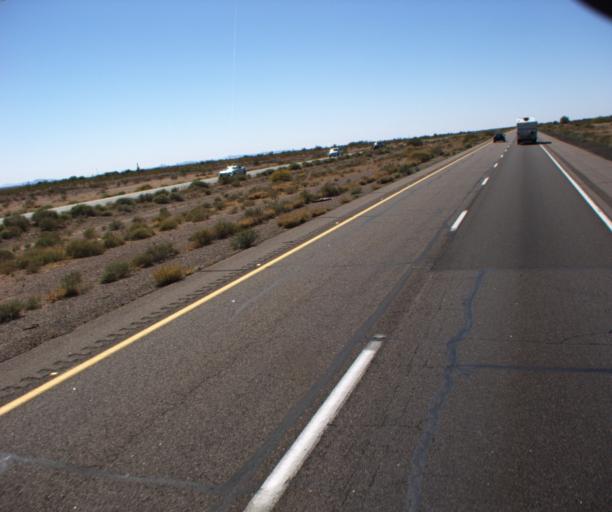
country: US
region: Arizona
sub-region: Maricopa County
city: Gila Bend
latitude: 32.8995
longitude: -113.0144
